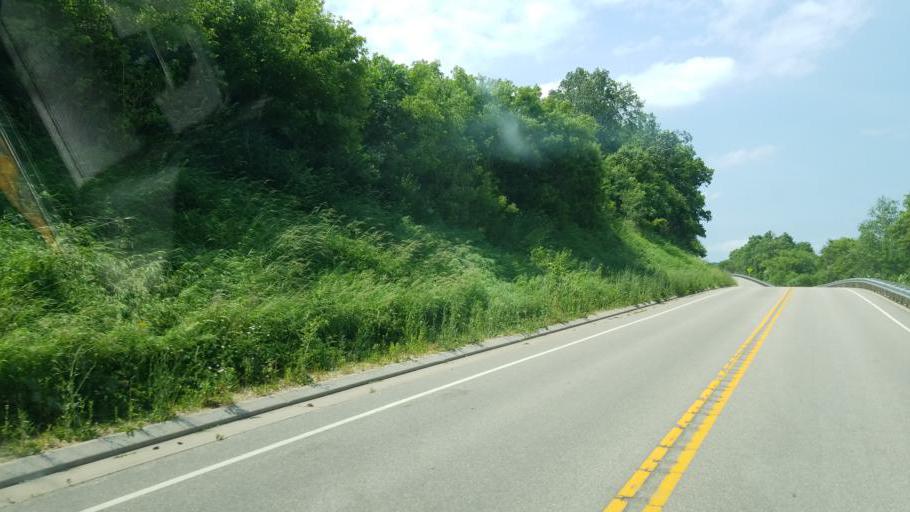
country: US
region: Wisconsin
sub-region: Vernon County
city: Westby
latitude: 43.5386
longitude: -90.6645
